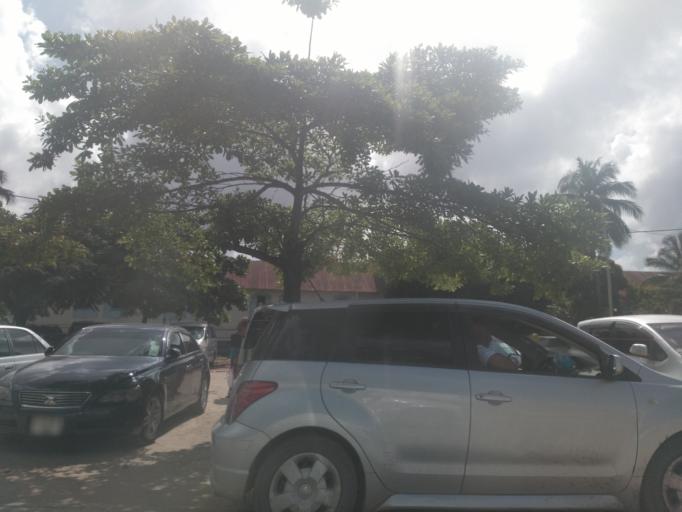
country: TZ
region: Zanzibar Urban/West
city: Zanzibar
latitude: -6.1614
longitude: 39.1944
